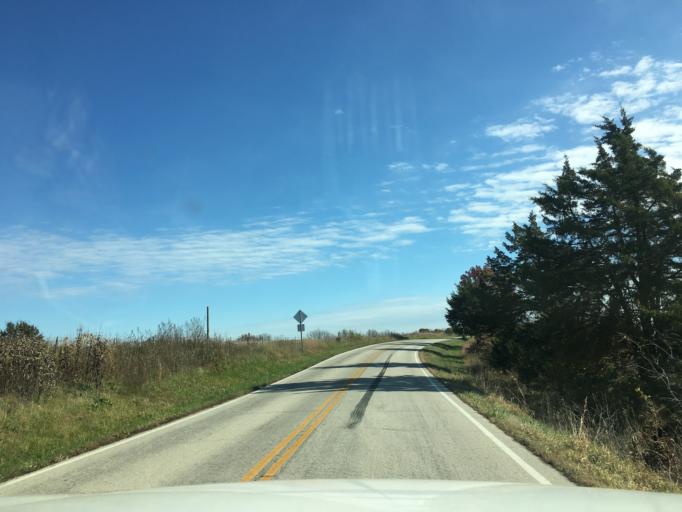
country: US
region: Missouri
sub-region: Osage County
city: Linn
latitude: 38.4191
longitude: -91.8236
